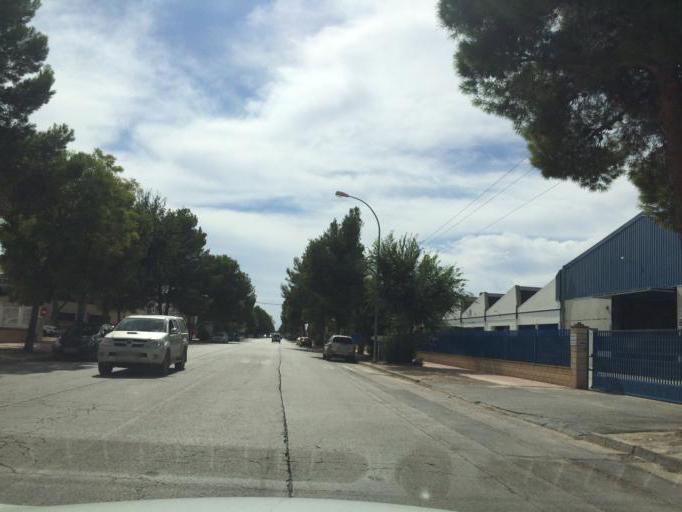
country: ES
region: Castille-La Mancha
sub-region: Provincia de Albacete
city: Albacete
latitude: 39.0126
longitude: -1.8816
